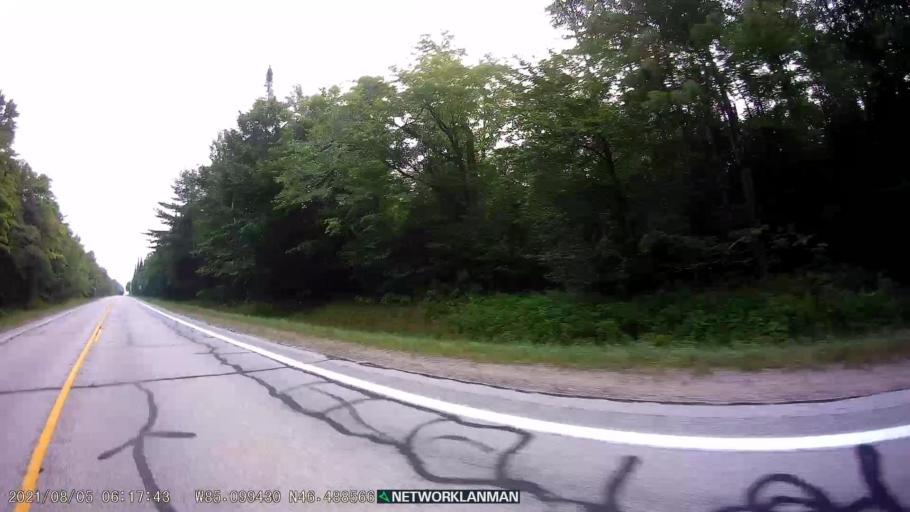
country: US
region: Michigan
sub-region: Luce County
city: Newberry
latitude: 46.4903
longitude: -85.0988
